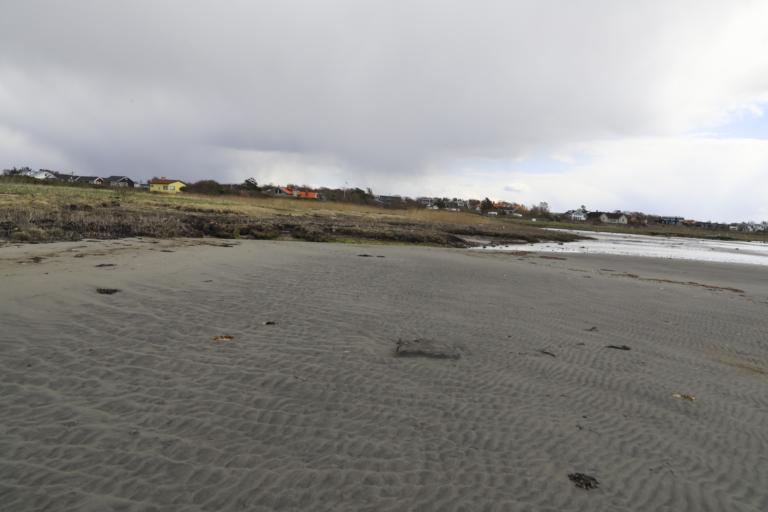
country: SE
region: Halland
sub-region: Varbergs Kommun
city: Traslovslage
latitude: 57.0753
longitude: 12.2587
